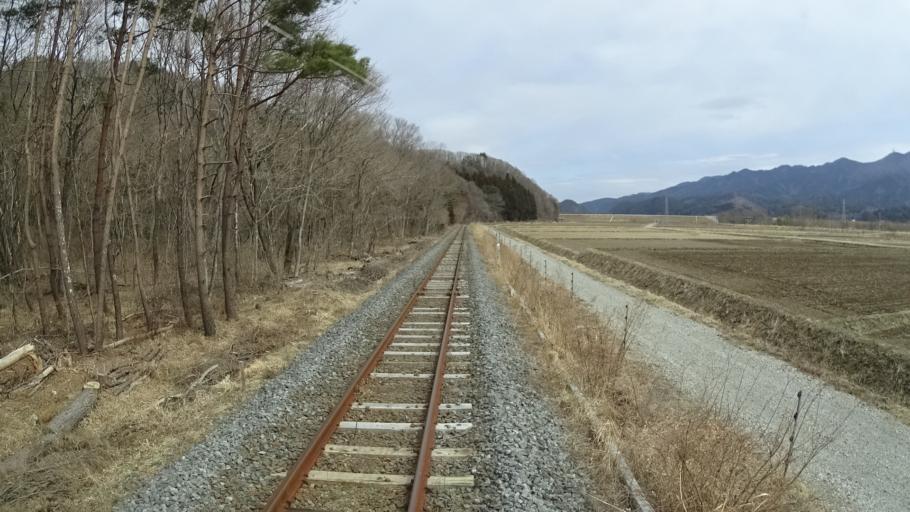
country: JP
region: Iwate
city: Yamada
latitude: 39.5202
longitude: 141.9167
